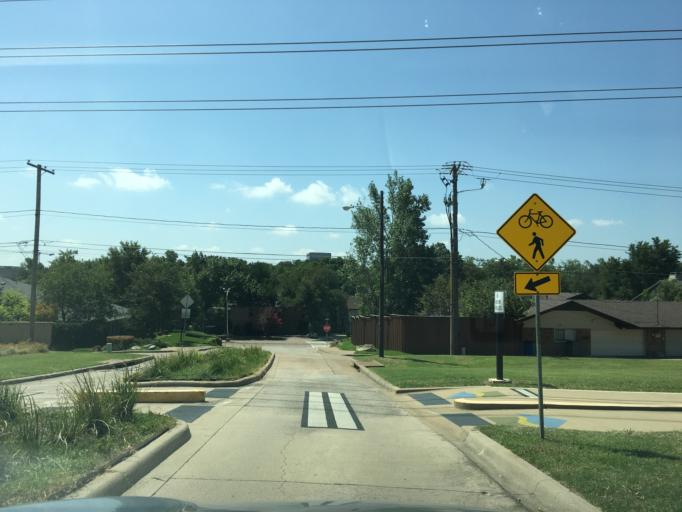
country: US
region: Texas
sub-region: Dallas County
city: University Park
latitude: 32.8985
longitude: -96.7745
